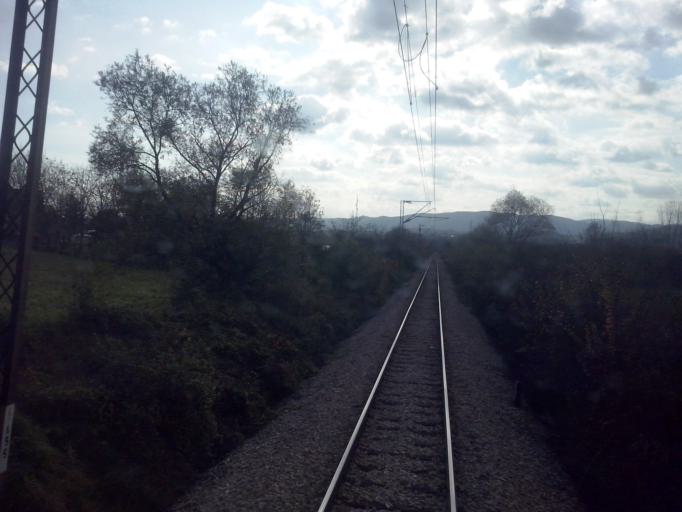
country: RS
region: Central Serbia
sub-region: Zlatiborski Okrug
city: Pozega
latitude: 43.8598
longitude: 20.0155
